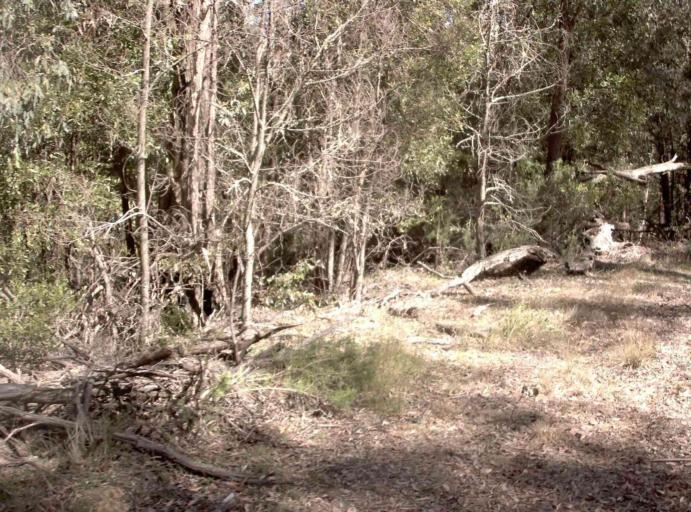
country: AU
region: New South Wales
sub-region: Bombala
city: Bombala
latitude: -37.1454
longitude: 148.7234
